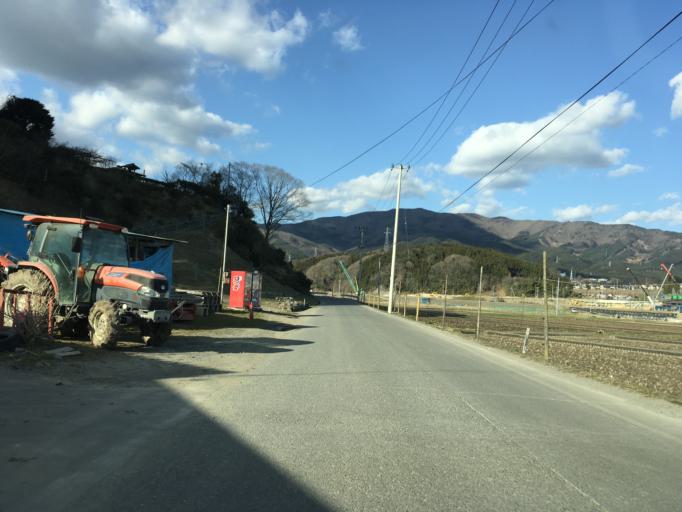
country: JP
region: Iwate
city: Ofunato
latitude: 39.0176
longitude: 141.6149
